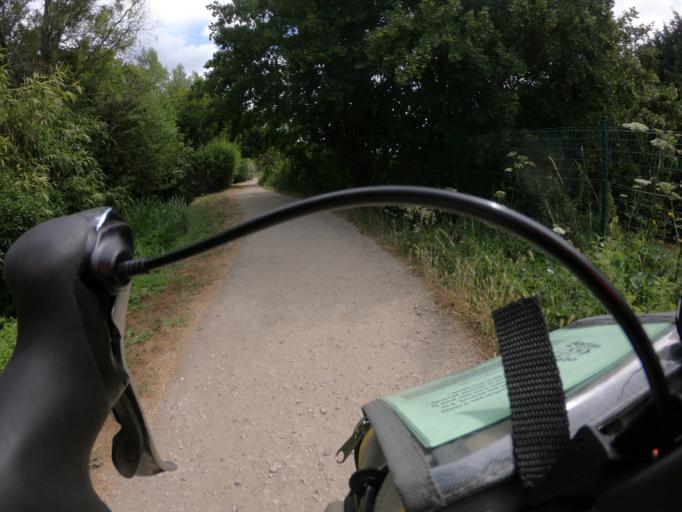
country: FR
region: Ile-de-France
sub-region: Departement de l'Essonne
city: Igny
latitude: 48.7384
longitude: 2.2396
